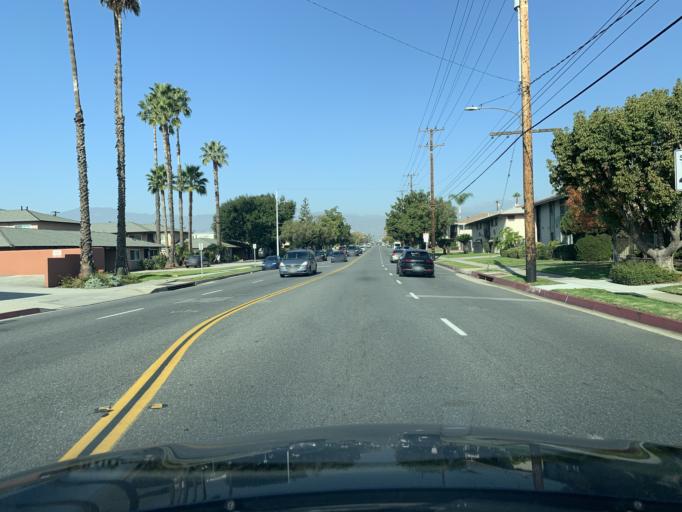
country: US
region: California
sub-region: Los Angeles County
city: Covina
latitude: 34.0794
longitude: -117.8813
